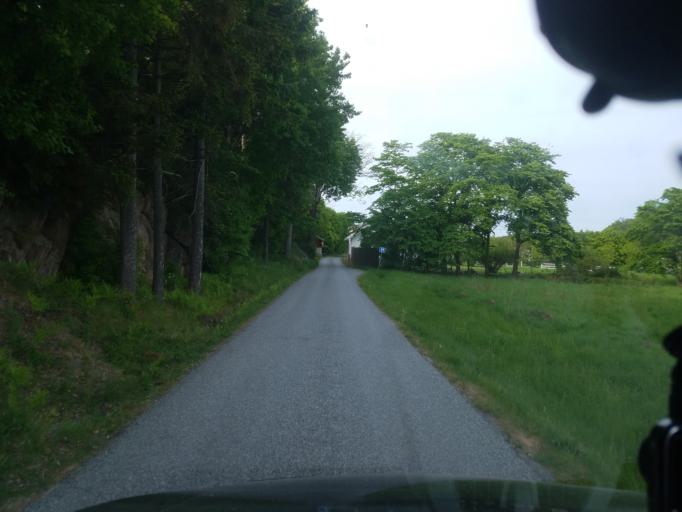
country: SE
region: Vaestra Goetaland
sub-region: Lysekils Kommun
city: Lysekil
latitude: 58.3016
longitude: 11.4521
